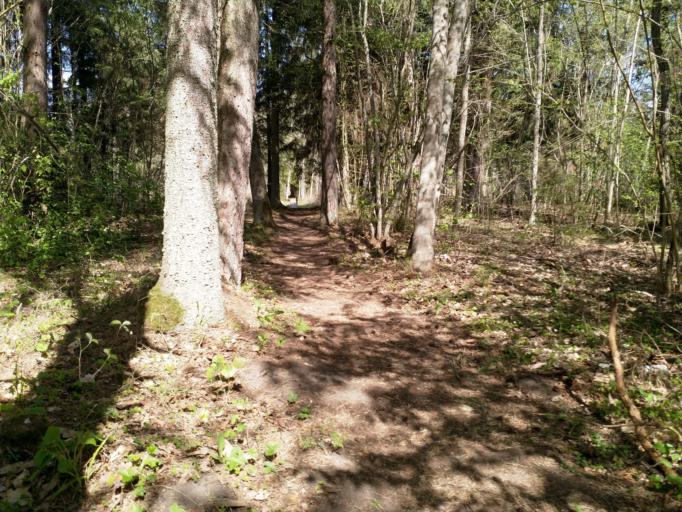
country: LV
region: Kandava
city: Kandava
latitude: 57.0207
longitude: 22.7738
